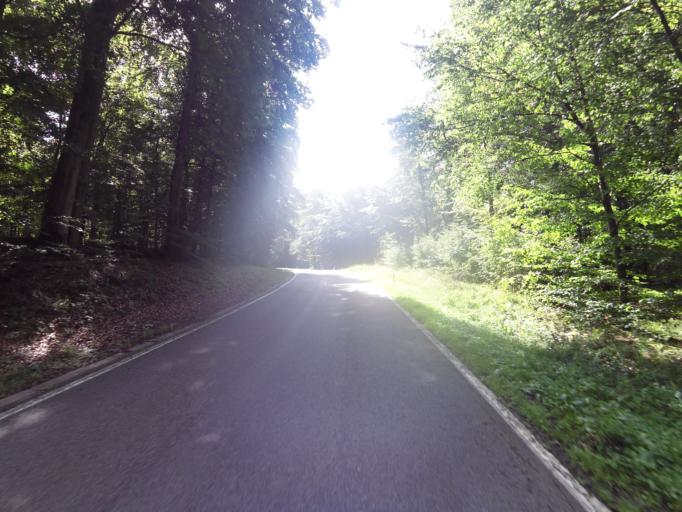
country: BE
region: Wallonia
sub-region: Province du Luxembourg
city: Saint-Hubert
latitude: 50.0636
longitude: 5.3453
